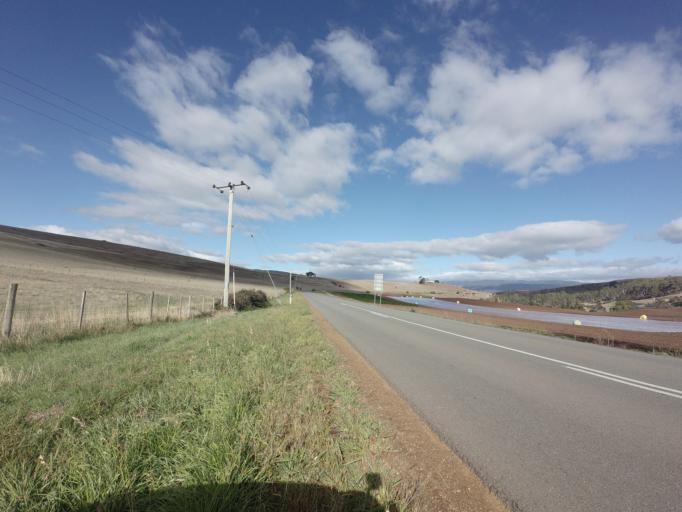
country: AU
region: Tasmania
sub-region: Derwent Valley
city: New Norfolk
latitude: -42.6947
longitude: 146.9334
